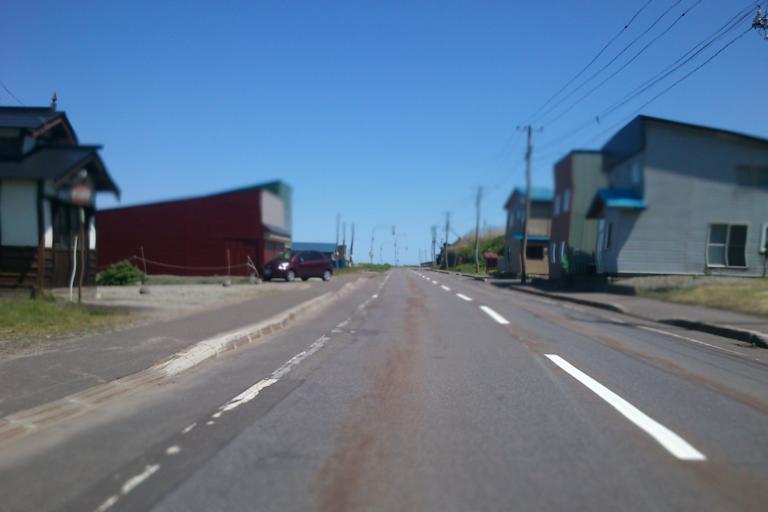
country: JP
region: Hokkaido
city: Rumoi
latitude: 43.8393
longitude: 141.4985
